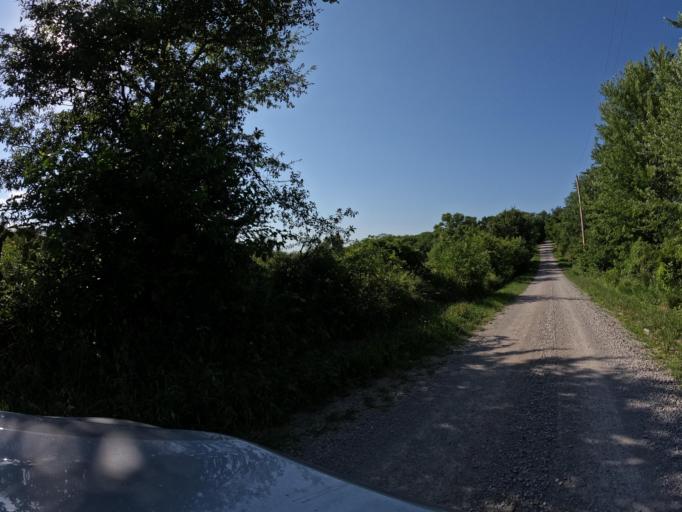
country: US
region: Iowa
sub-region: Appanoose County
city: Centerville
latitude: 40.7287
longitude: -93.0159
